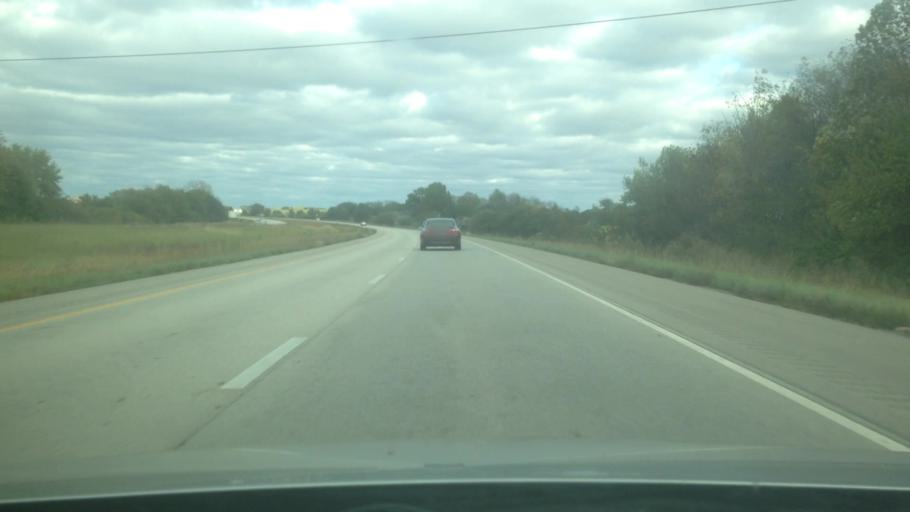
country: US
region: Illinois
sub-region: Macon County
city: Forsyth
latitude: 39.9112
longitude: -88.8751
